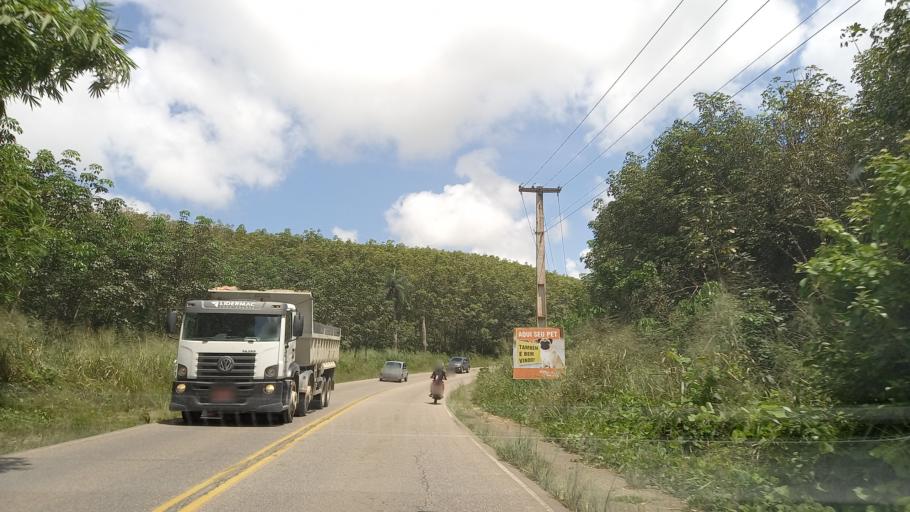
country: BR
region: Pernambuco
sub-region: Rio Formoso
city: Rio Formoso
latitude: -8.6509
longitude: -35.1317
